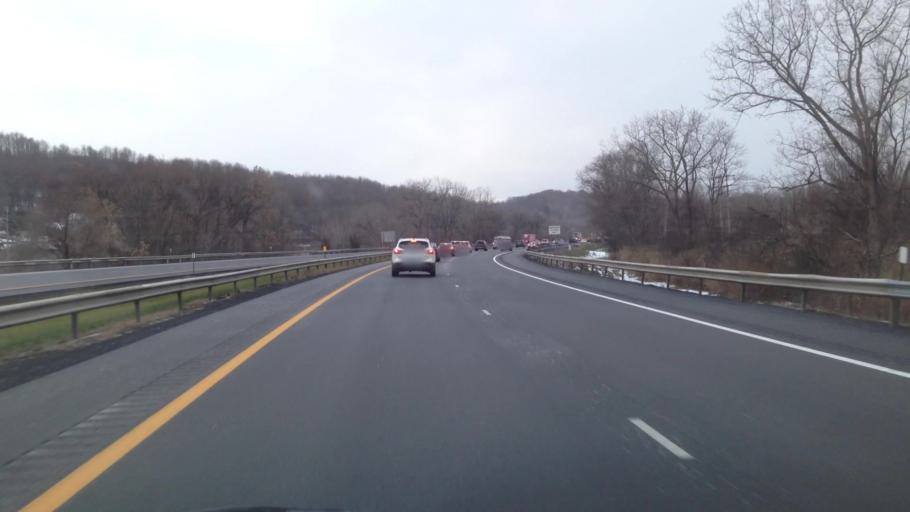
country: US
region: New York
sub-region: Montgomery County
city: Canajoharie
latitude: 42.9063
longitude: -74.5838
